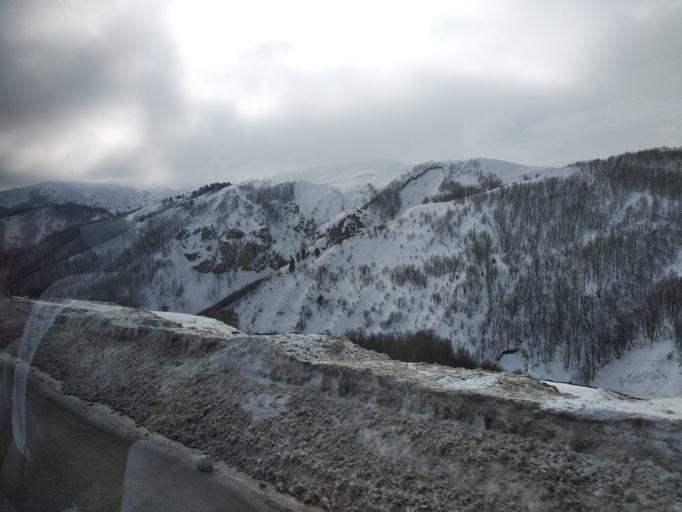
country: TR
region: Erzincan
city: Catalarmut
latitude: 39.8944
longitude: 39.3792
